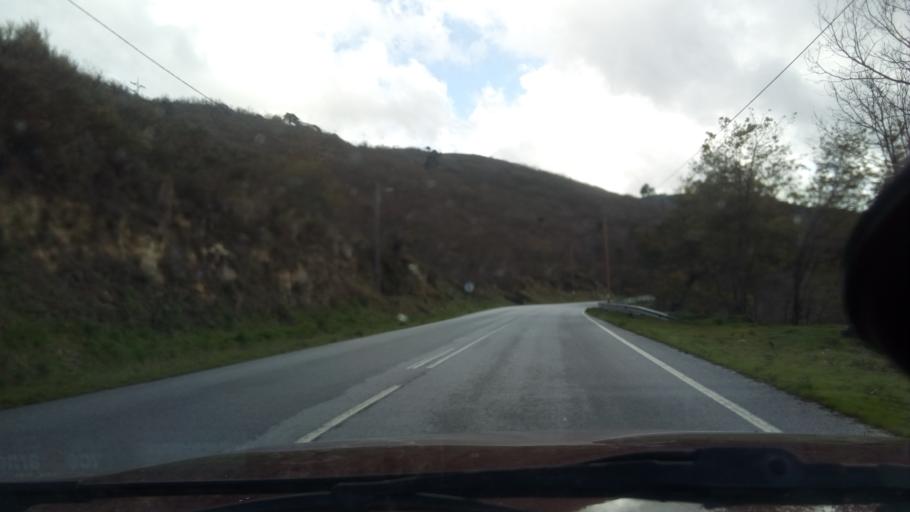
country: PT
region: Guarda
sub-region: Guarda
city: Guarda
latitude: 40.5663
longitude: -7.2981
